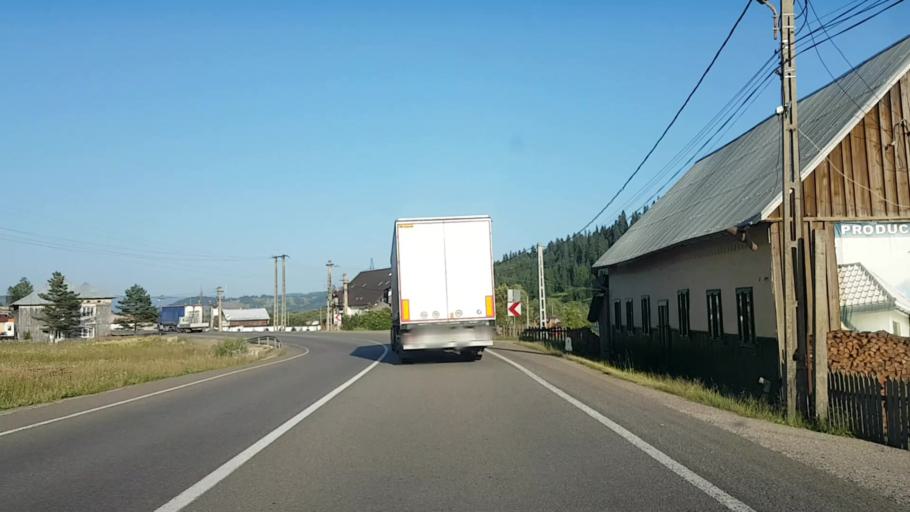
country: RO
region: Suceava
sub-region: Comuna Cosna
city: Cosna
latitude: 47.3610
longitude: 25.1959
